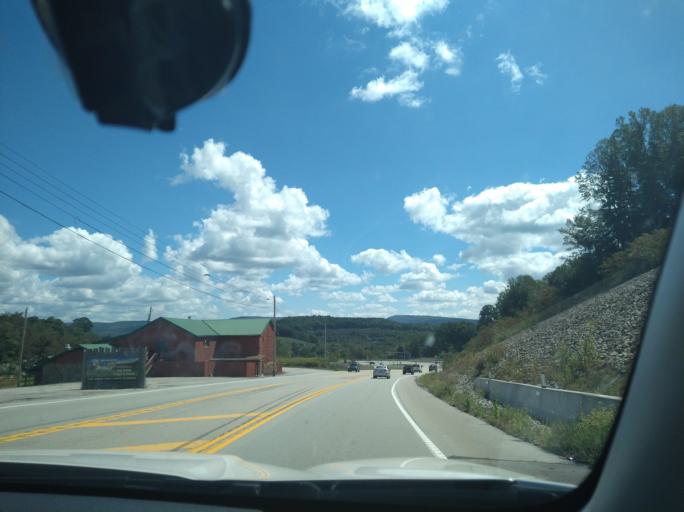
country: US
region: Pennsylvania
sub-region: Fayette County
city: Bear Rocks
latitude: 40.1103
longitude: -79.3853
